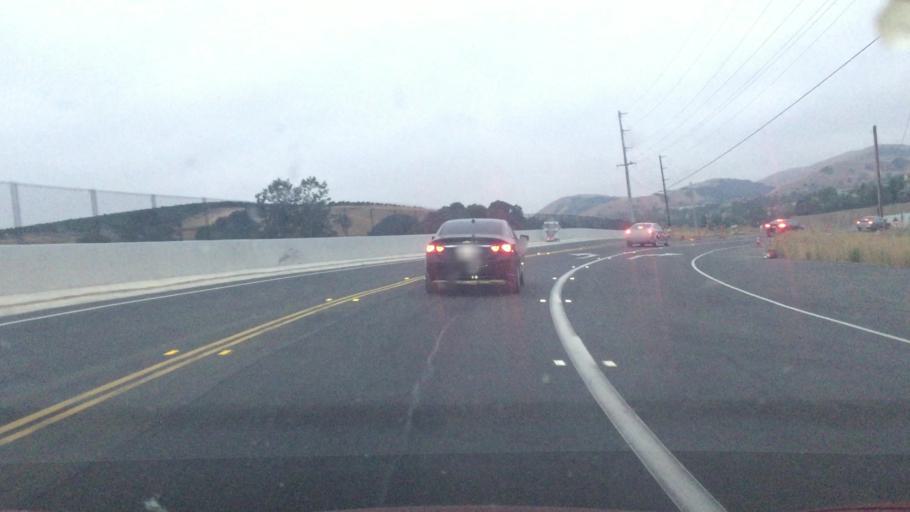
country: US
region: California
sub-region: Alameda County
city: Livermore
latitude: 37.6378
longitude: -121.7972
